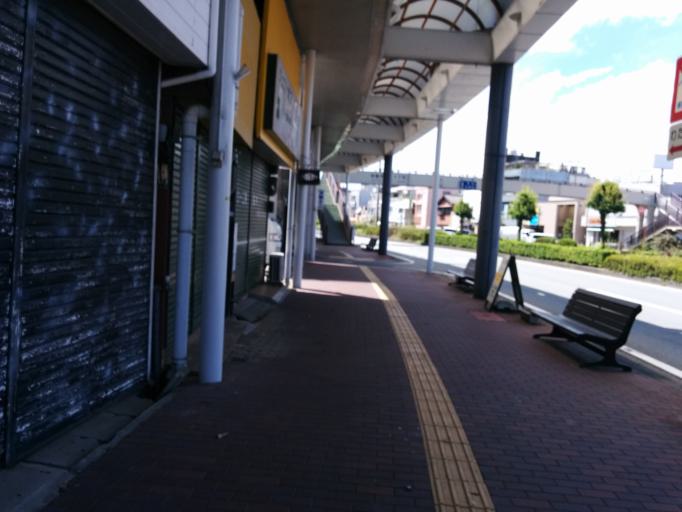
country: JP
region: Mie
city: Ise
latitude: 34.4929
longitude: 136.7077
